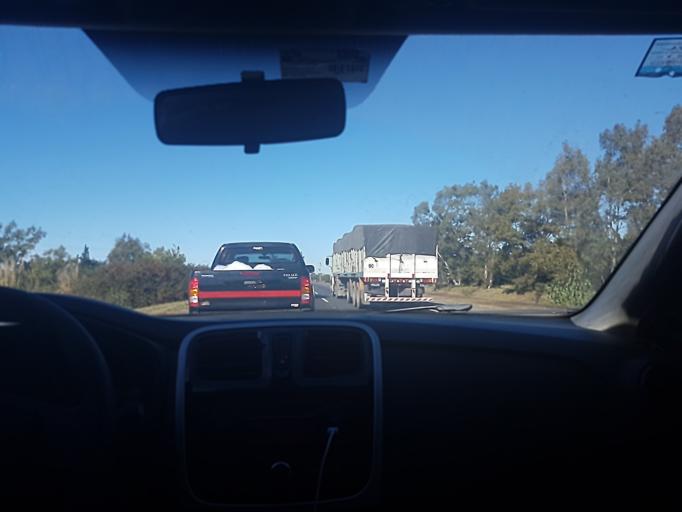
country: AR
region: Cordoba
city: Pilar
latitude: -31.6418
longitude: -63.8652
